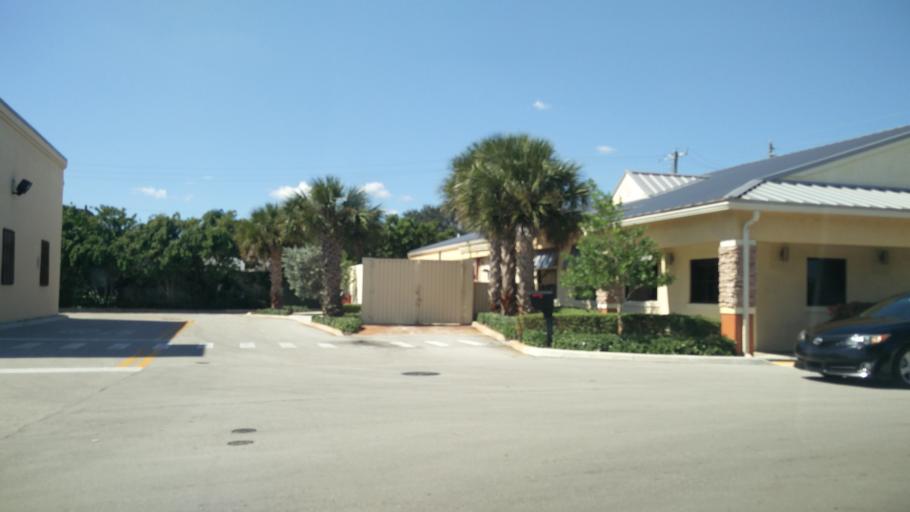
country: US
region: Florida
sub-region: Broward County
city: Cooper City
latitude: 26.0640
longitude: -80.2537
